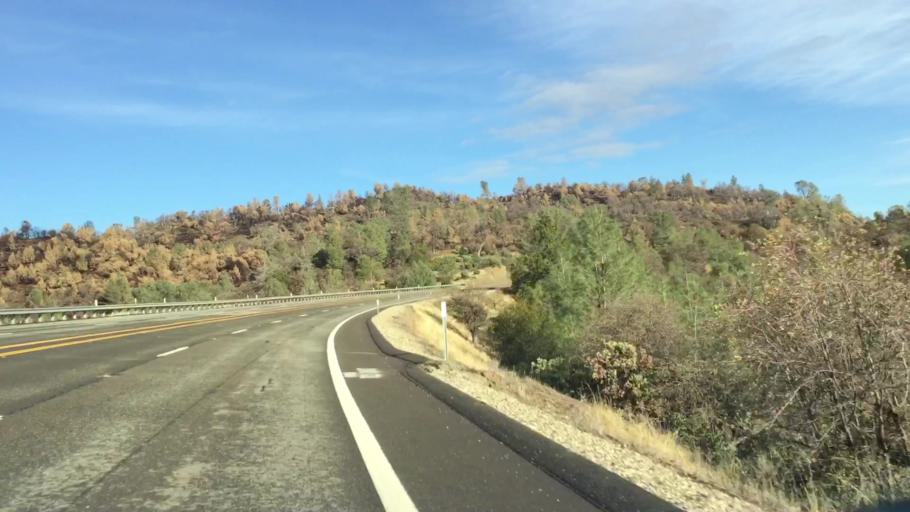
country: US
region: California
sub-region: Butte County
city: Paradise
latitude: 39.6836
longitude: -121.5395
